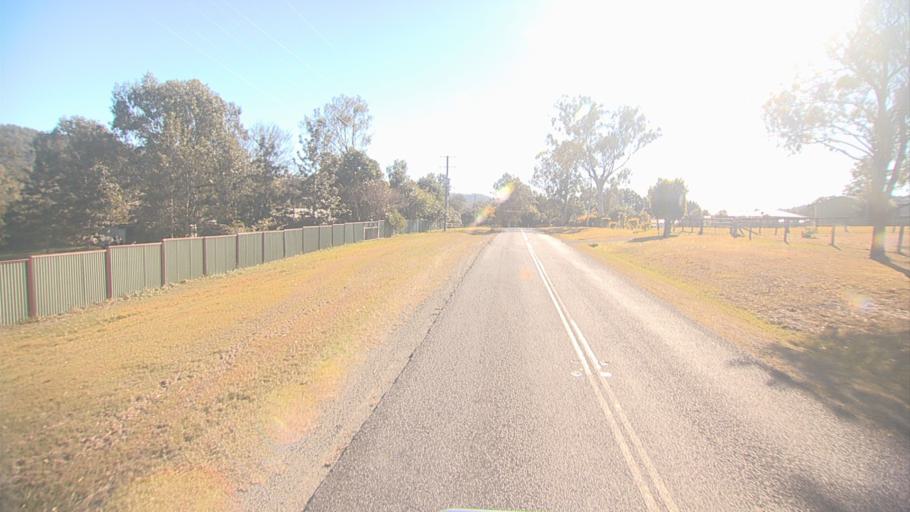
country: AU
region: Queensland
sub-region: Logan
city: Windaroo
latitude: -27.8109
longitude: 153.1706
